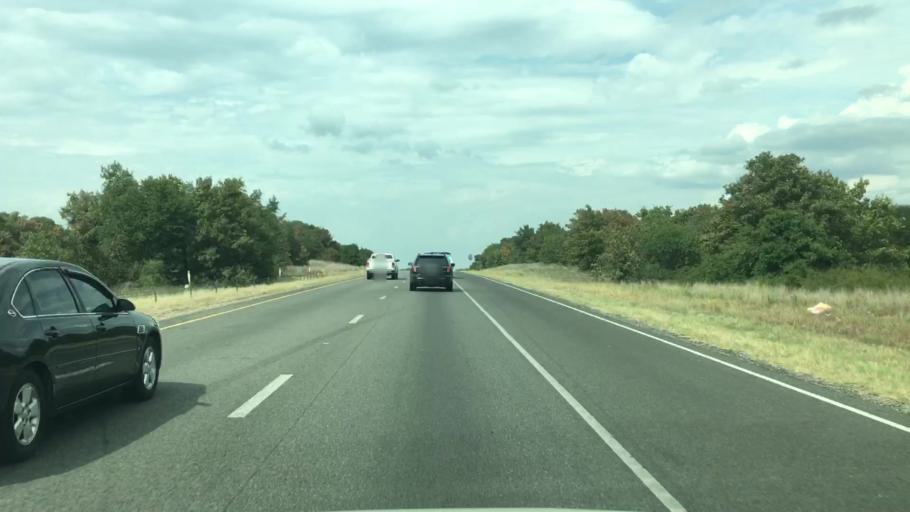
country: US
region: Texas
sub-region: Bexar County
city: Elmendorf
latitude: 29.1866
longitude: -98.4246
